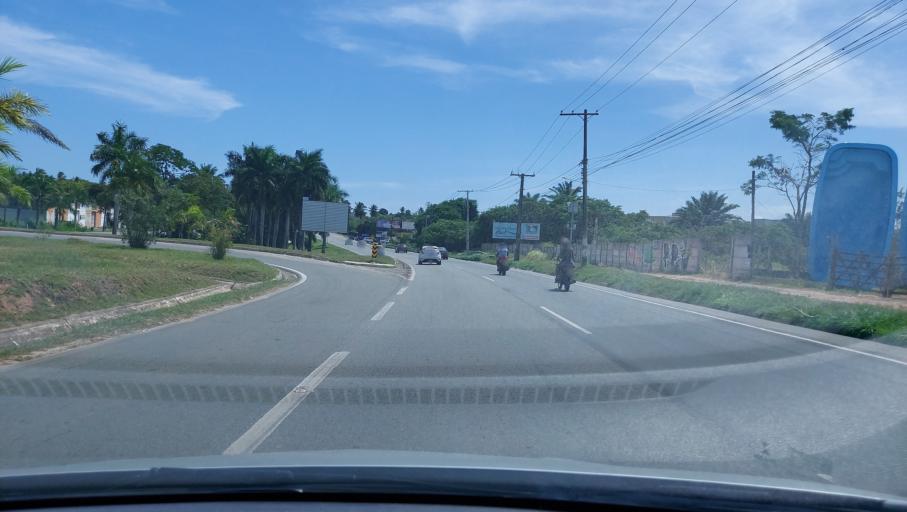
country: BR
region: Bahia
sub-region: Lauro De Freitas
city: Lauro de Freitas
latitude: -12.8429
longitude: -38.2778
